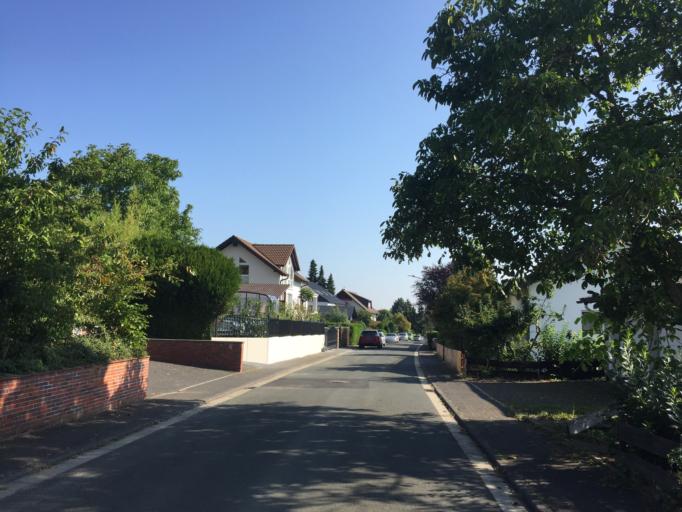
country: DE
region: Hesse
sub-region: Regierungsbezirk Giessen
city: Schoeffengrund
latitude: 50.4515
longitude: 8.5528
